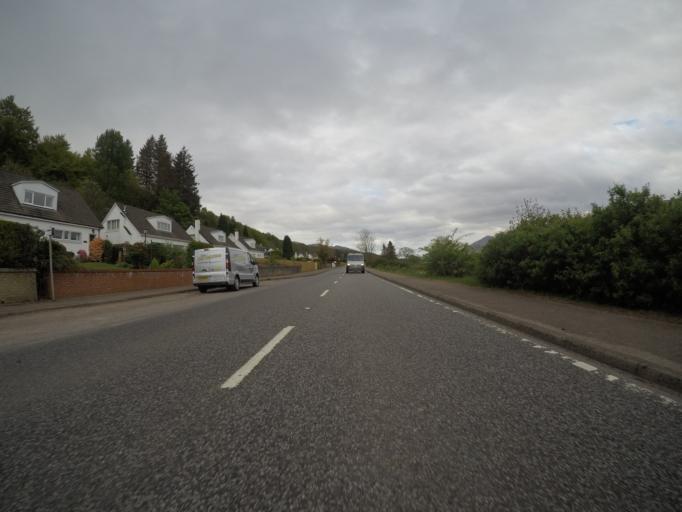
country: GB
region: Scotland
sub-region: Highland
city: Fort William
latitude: 56.7998
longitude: -5.1368
